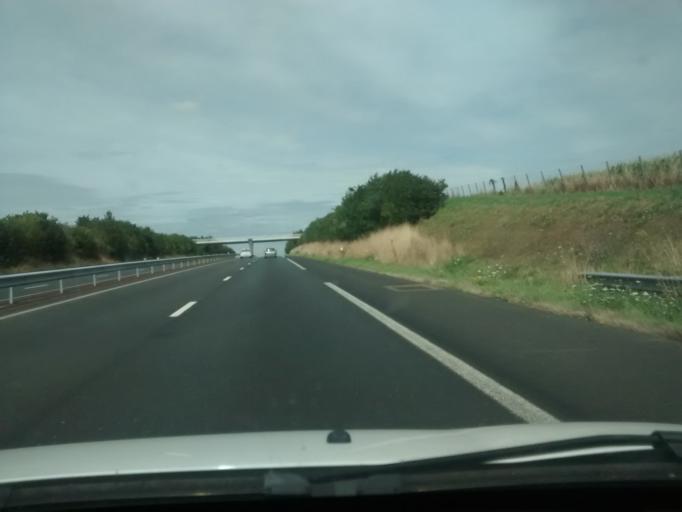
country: FR
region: Lower Normandy
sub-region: Departement de la Manche
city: Ducey
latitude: 48.5998
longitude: -1.3309
